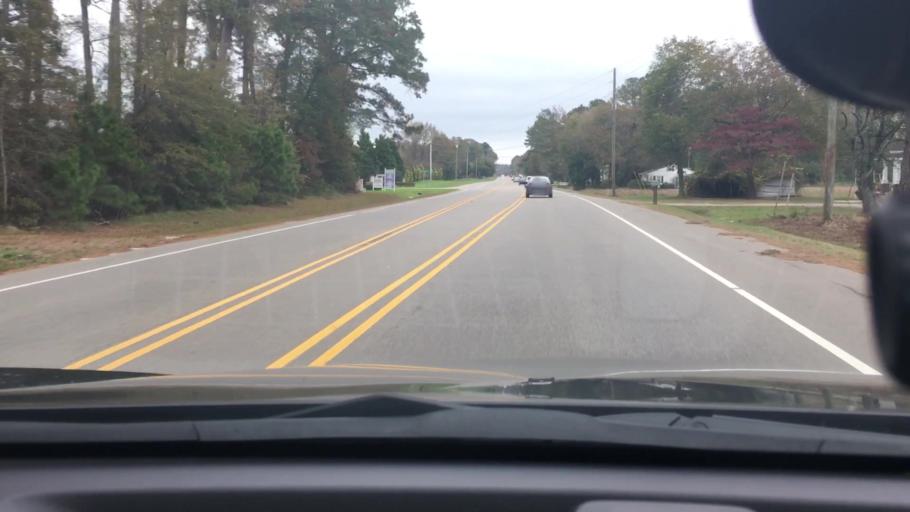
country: US
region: North Carolina
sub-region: Pitt County
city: Summerfield
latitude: 35.5792
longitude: -77.4253
